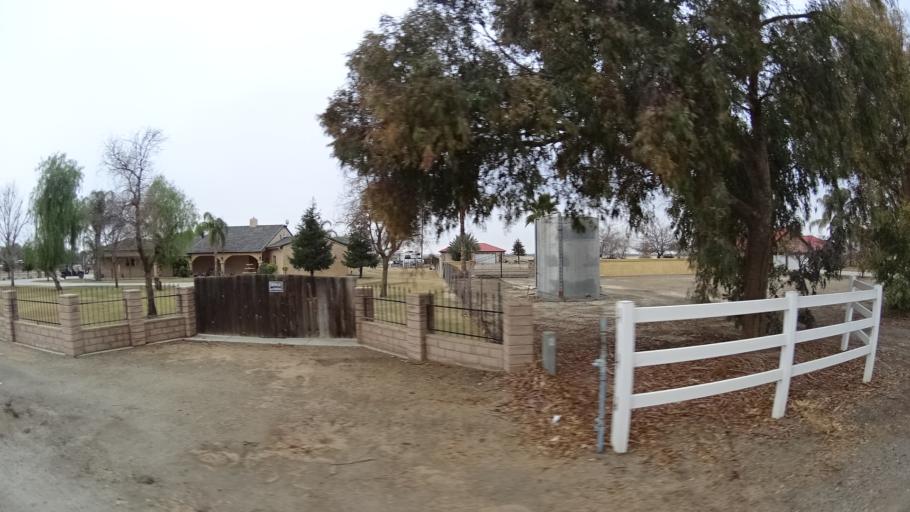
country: US
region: California
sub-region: Kern County
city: Lamont
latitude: 35.3243
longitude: -118.9410
